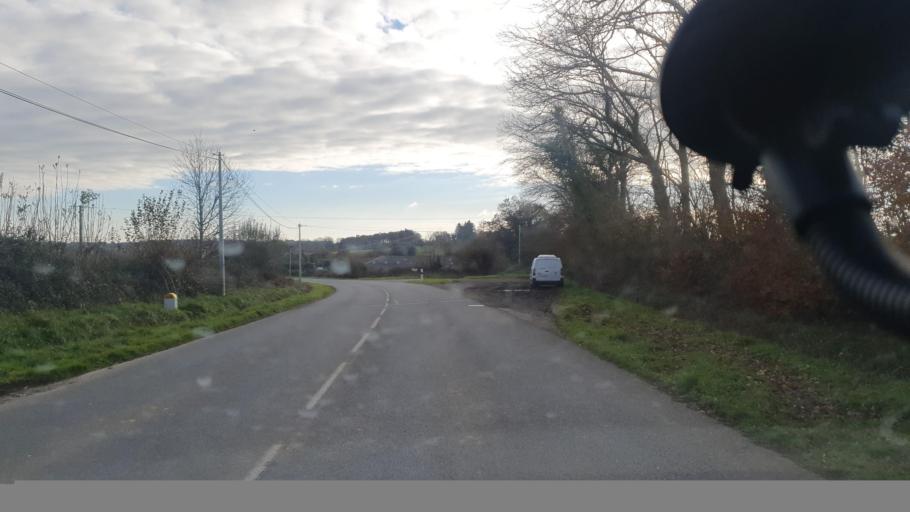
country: FR
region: Brittany
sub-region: Departement du Finistere
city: Edern
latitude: 48.0941
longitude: -3.9837
